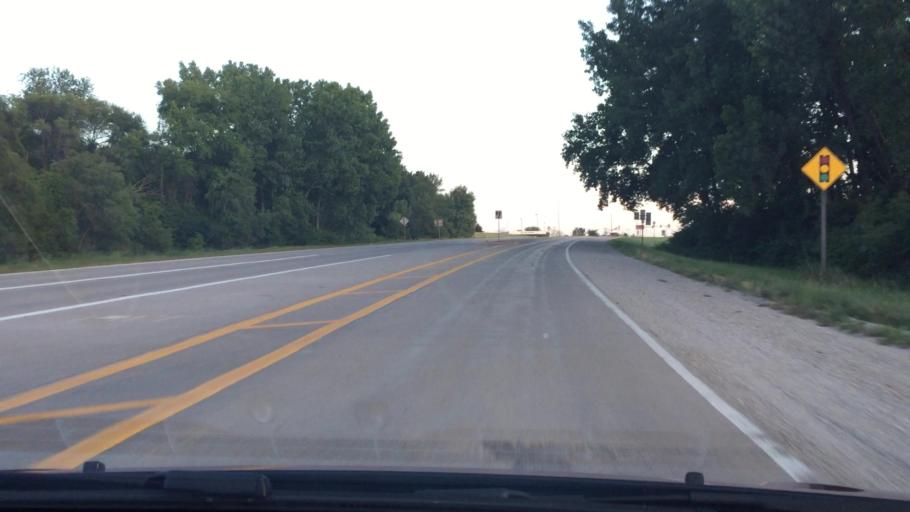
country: US
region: Iowa
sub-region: Muscatine County
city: Muscatine
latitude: 41.4579
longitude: -91.0306
